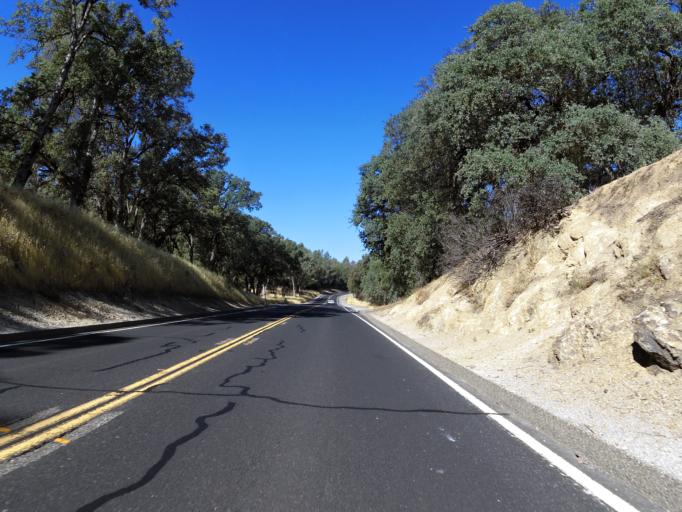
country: US
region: California
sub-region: Mariposa County
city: Mariposa
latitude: 37.4777
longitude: -120.0339
